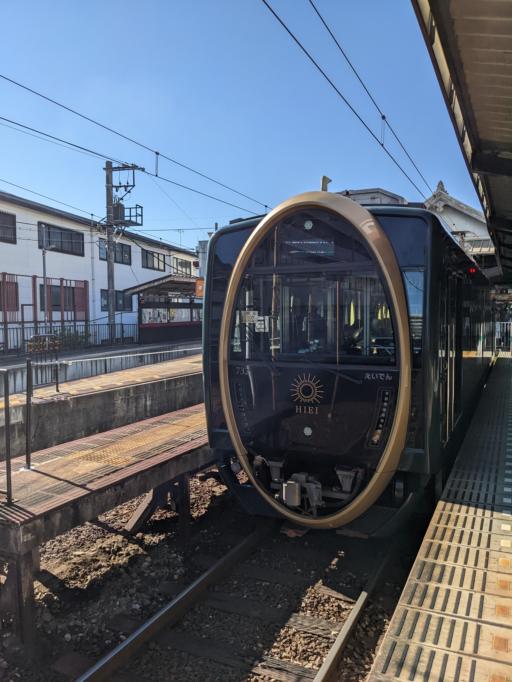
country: JP
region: Kyoto
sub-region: Kyoto-shi
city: Kamigyo-ku
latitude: 35.0307
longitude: 135.7734
